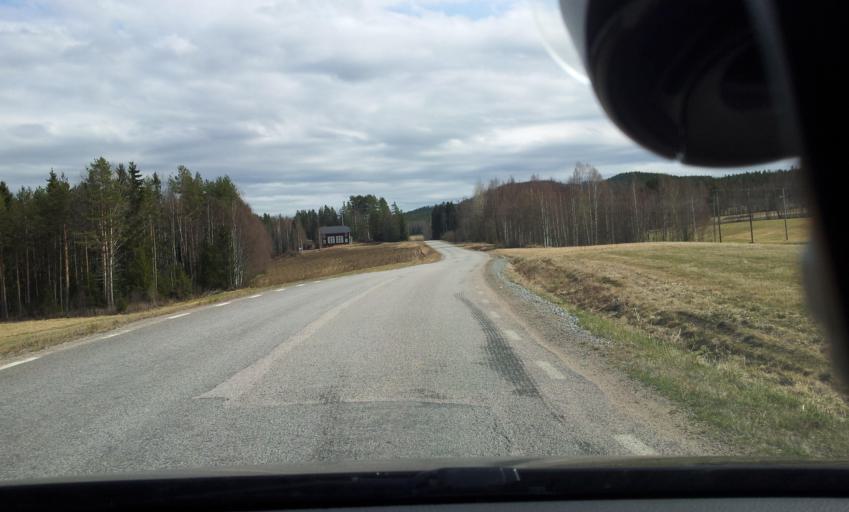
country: SE
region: Gaevleborg
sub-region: Ljusdals Kommun
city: Farila
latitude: 61.7702
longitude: 15.9688
